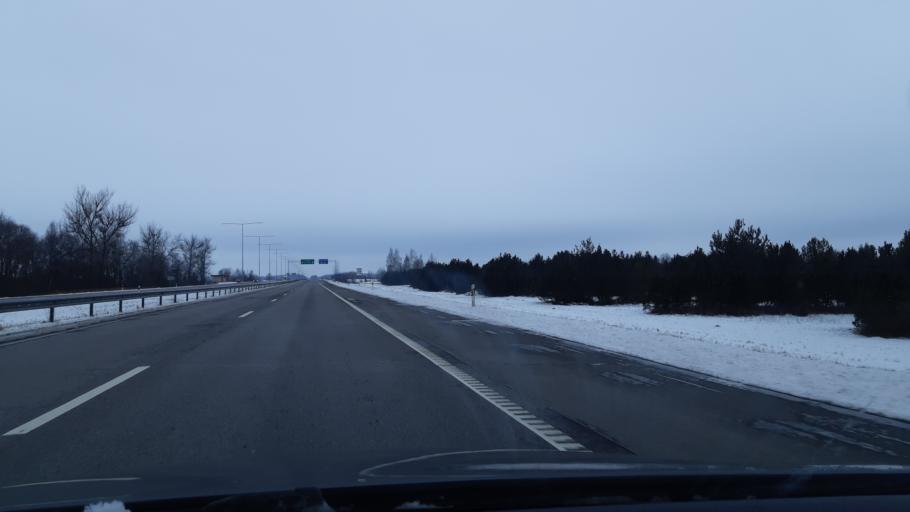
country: LT
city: Vilkija
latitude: 55.1349
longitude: 23.7314
